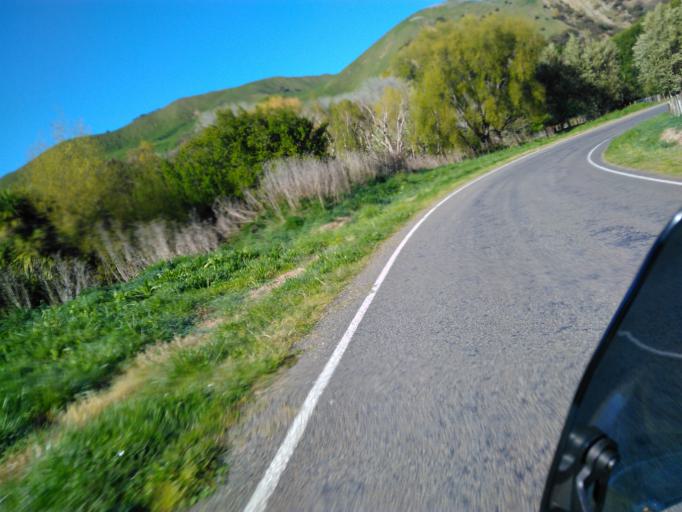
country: NZ
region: Gisborne
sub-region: Gisborne District
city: Gisborne
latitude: -38.4281
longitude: 177.7302
